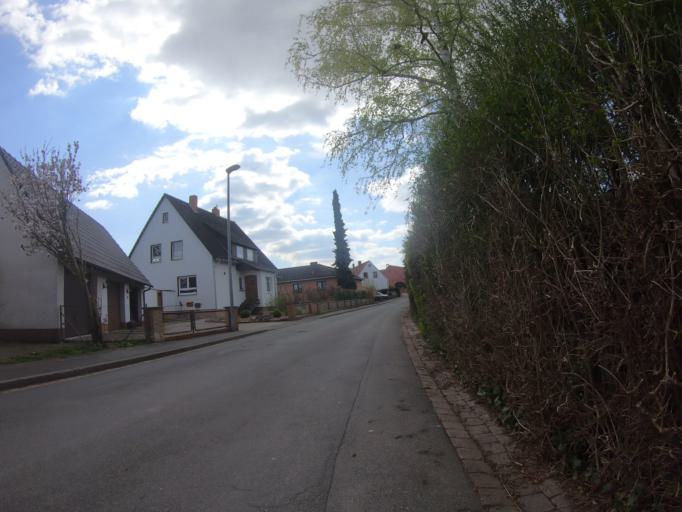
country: DE
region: Lower Saxony
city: Nordstemmen
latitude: 52.2163
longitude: 9.7974
